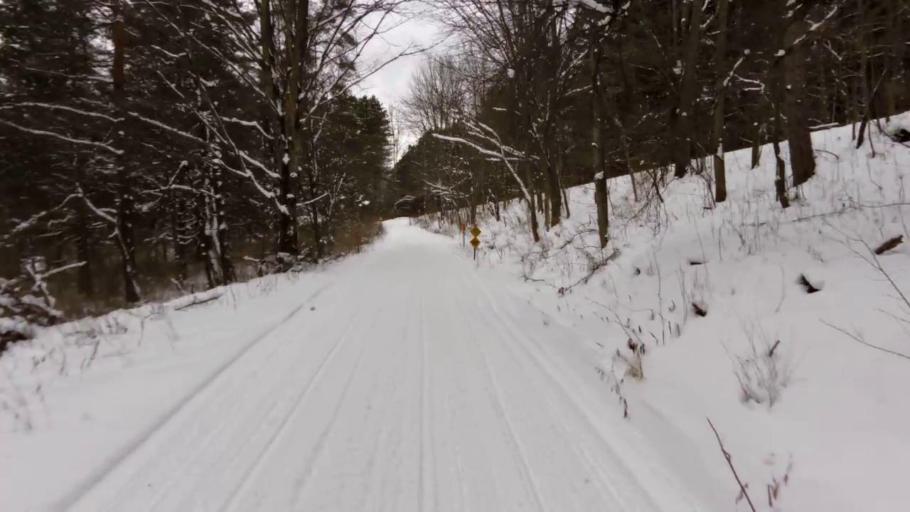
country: US
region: Pennsylvania
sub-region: McKean County
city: Bradford
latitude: 42.0272
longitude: -78.7219
